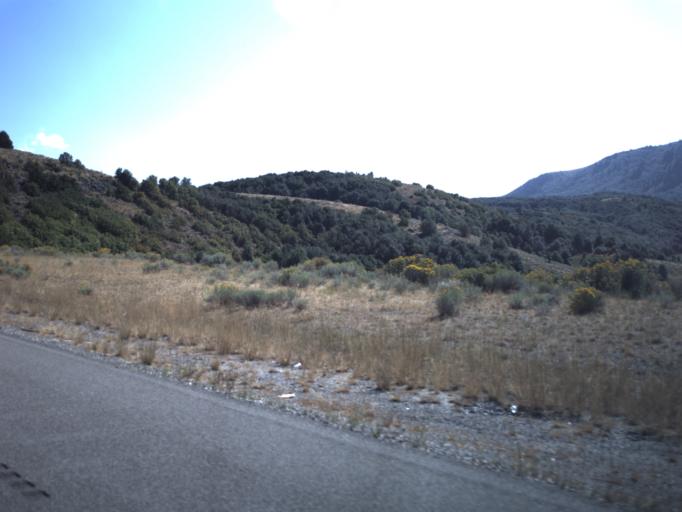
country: US
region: Utah
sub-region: Box Elder County
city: Brigham City
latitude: 41.5598
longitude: -111.9610
